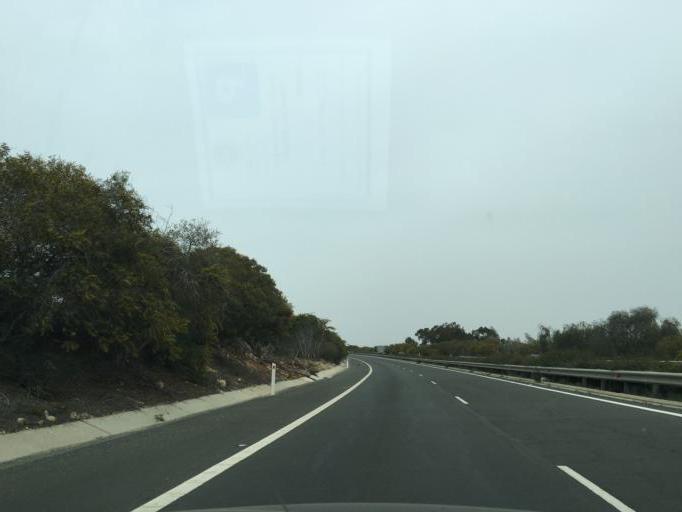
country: CY
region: Ammochostos
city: Ayia Napa
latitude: 34.9998
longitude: 33.9869
